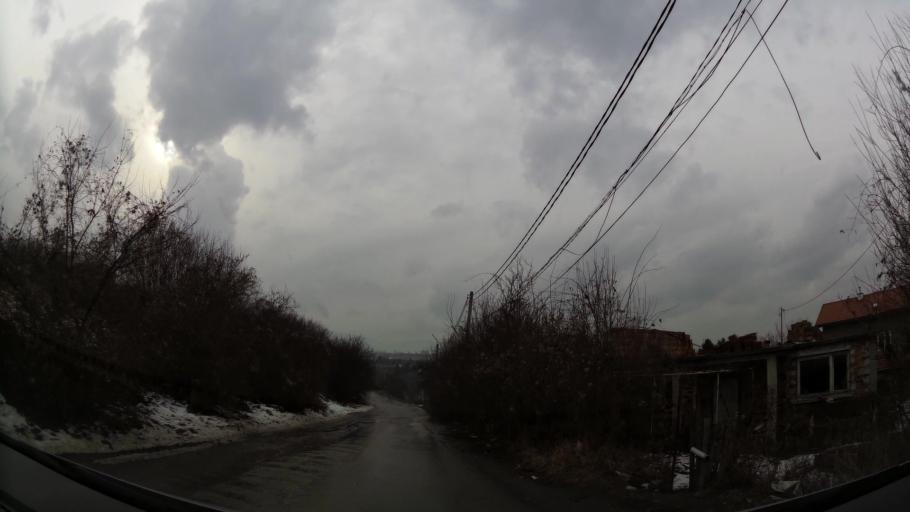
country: BG
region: Sofiya
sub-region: Obshtina Bozhurishte
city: Bozhurishte
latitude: 42.6953
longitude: 23.2208
